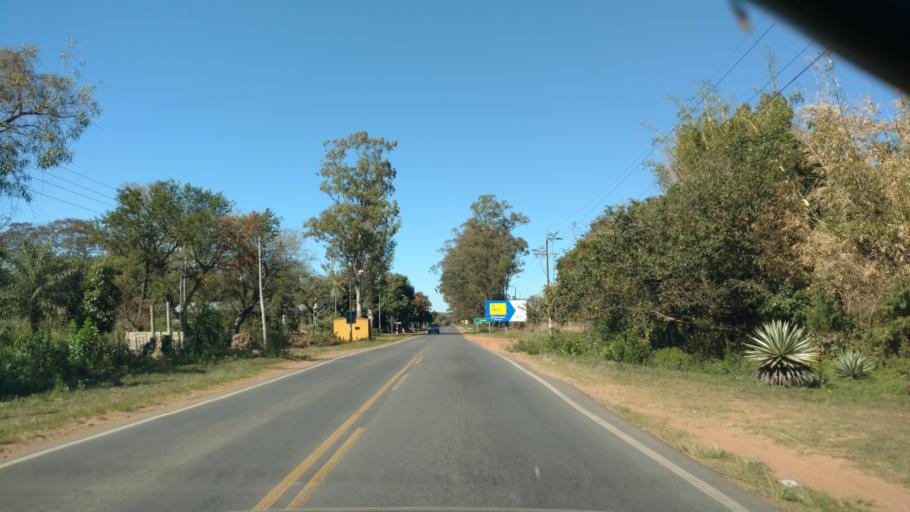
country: PY
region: Central
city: Ypacarai
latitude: -25.4418
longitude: -57.2771
